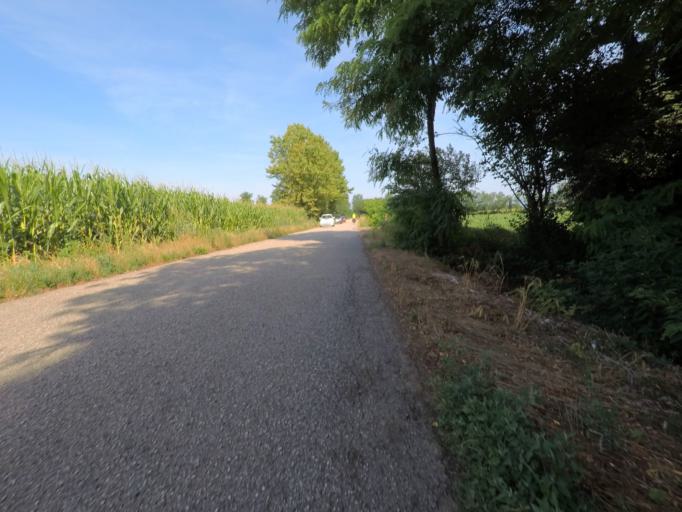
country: IT
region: Friuli Venezia Giulia
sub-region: Provincia di Udine
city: Colloredo di Prato
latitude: 46.0598
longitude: 13.1105
